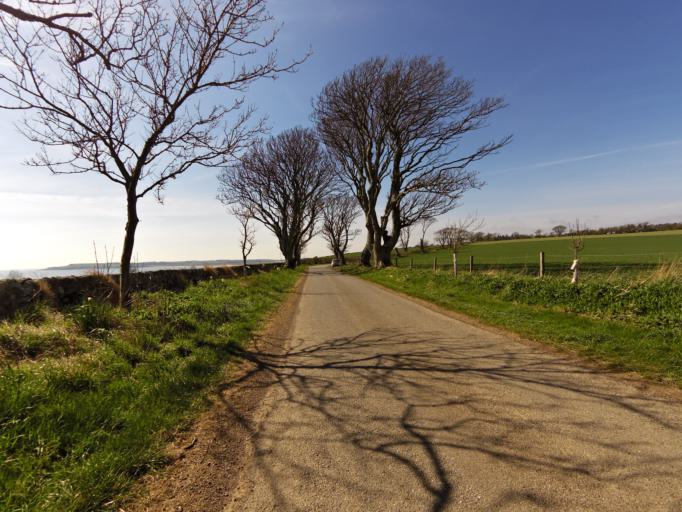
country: GB
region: Scotland
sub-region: Angus
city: Montrose
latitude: 56.6792
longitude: -2.4691
